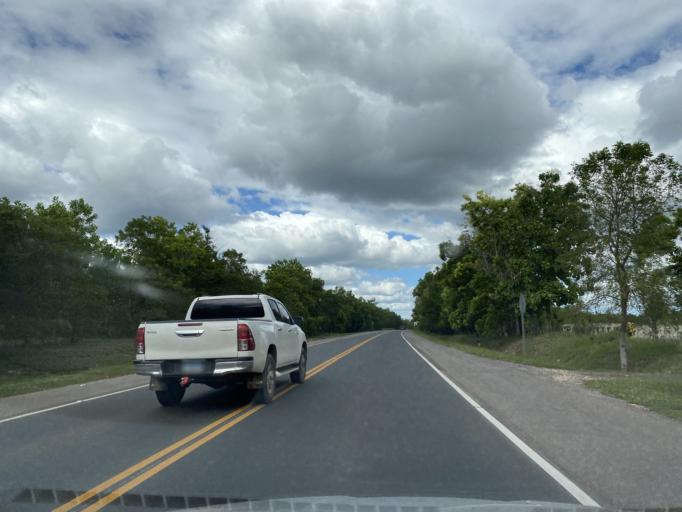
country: DO
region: Santo Domingo
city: Guerra
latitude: 18.6044
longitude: -69.7705
